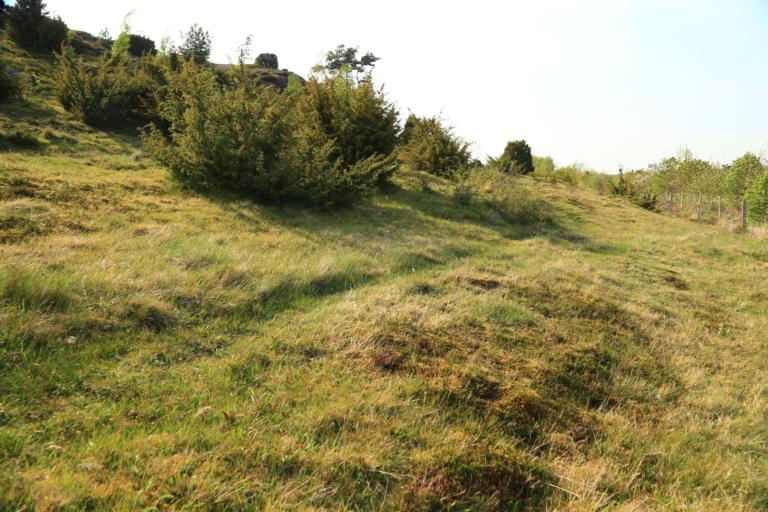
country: SE
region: Halland
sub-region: Varbergs Kommun
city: Varberg
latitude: 57.1602
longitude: 12.2406
